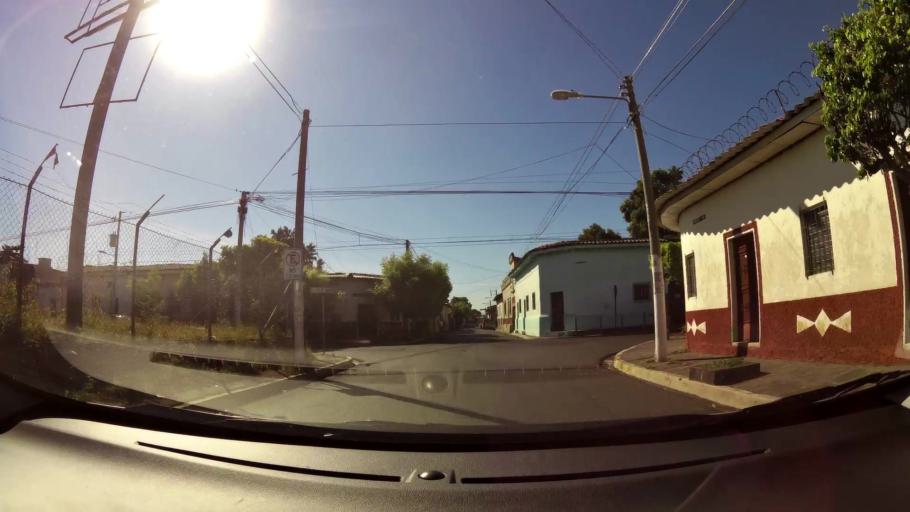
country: SV
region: San Miguel
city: San Miguel
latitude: 13.4765
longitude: -88.1753
